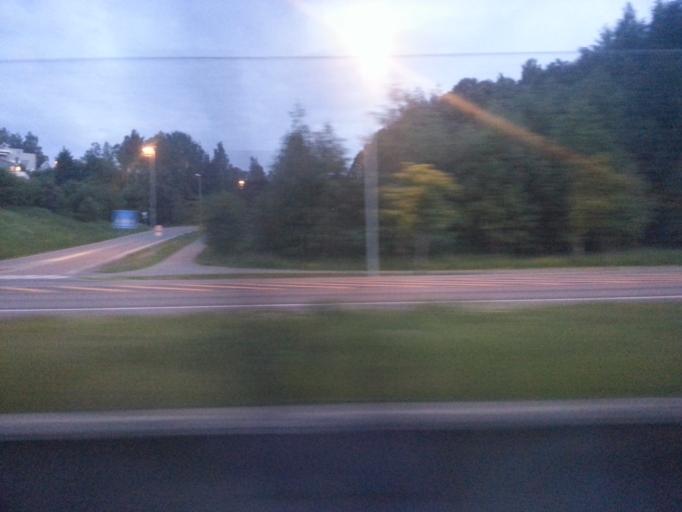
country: NO
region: Akershus
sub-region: Skedsmo
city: Lillestrom
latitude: 59.9524
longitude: 11.0285
